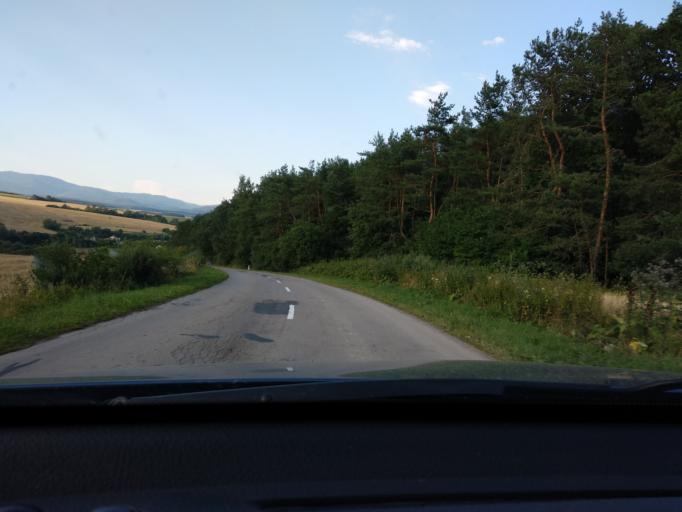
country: SK
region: Nitriansky
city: Banovce nad Bebravou
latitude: 48.7305
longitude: 18.1569
